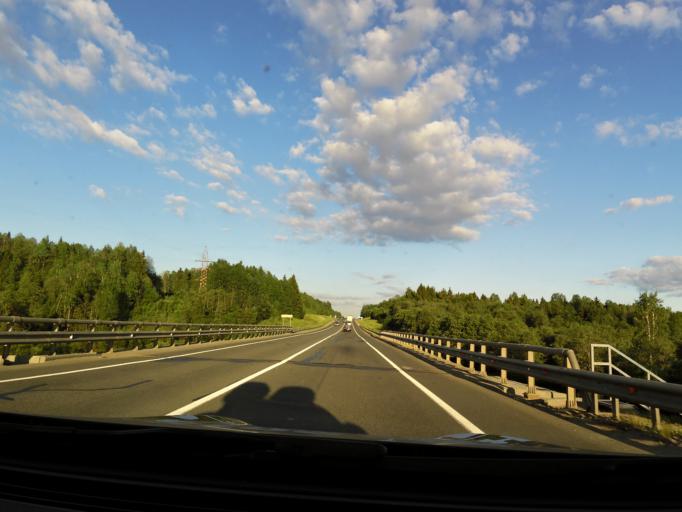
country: RU
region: Vologda
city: Gryazovets
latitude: 59.0526
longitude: 40.0784
